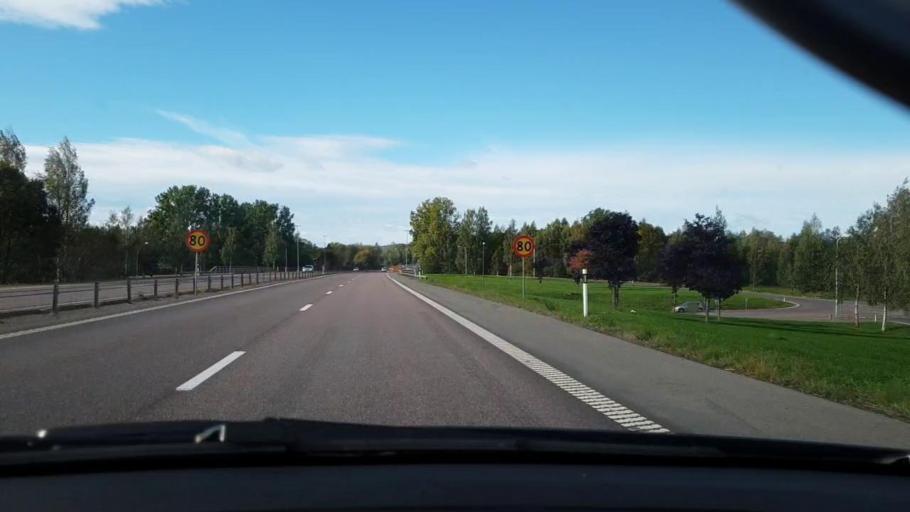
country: SE
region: Dalarna
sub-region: Borlange Kommun
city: Borlaenge
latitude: 60.4863
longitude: 15.4659
